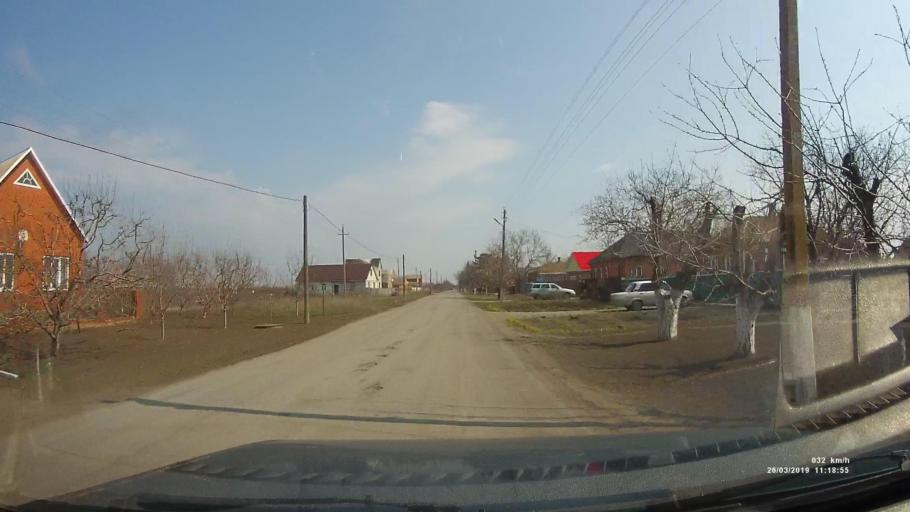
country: RU
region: Krasnodarskiy
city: Shabel'skoye
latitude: 47.1338
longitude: 38.5360
